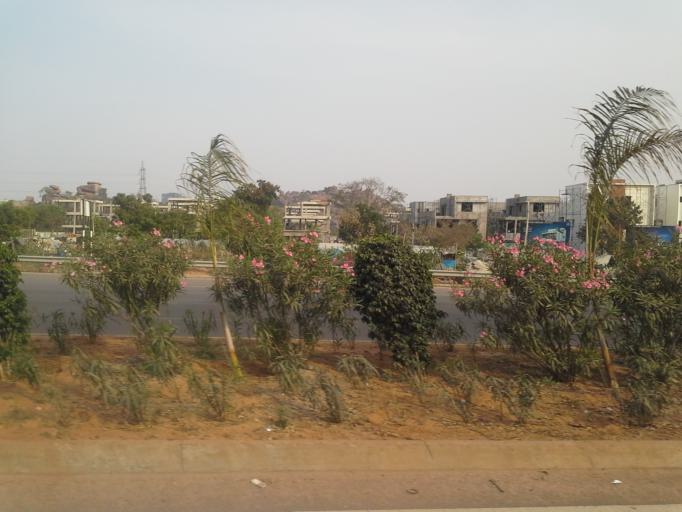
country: IN
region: Telangana
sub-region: Rangareddi
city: Kukatpalli
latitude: 17.4122
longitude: 78.3549
